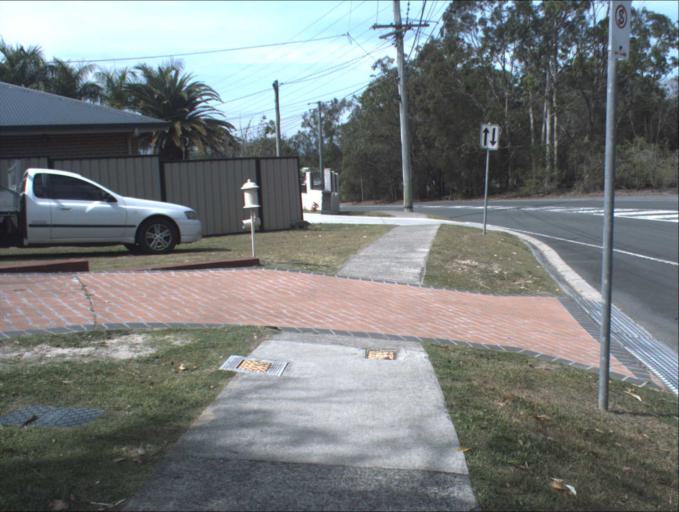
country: AU
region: Queensland
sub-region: Logan
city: Springwood
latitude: -27.6248
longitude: 153.1470
